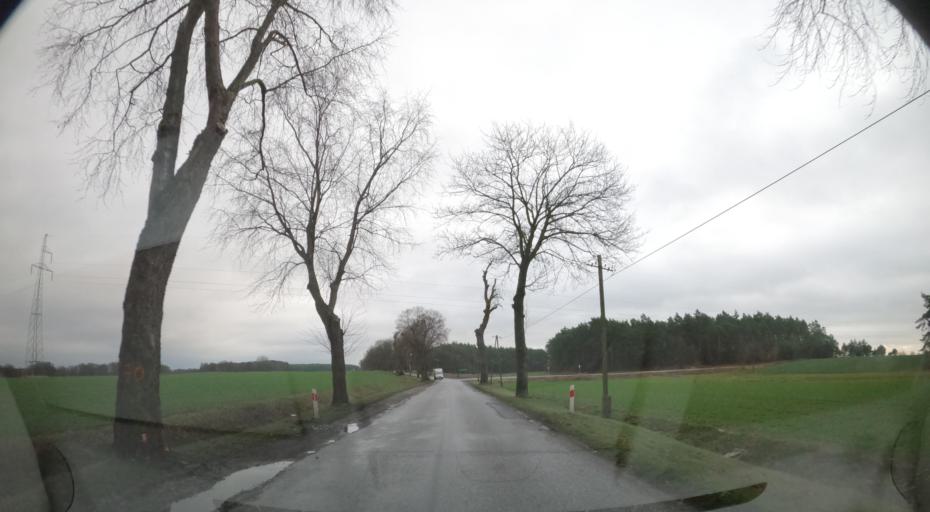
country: PL
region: Greater Poland Voivodeship
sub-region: Powiat zlotowski
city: Krajenka
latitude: 53.2872
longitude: 17.0024
